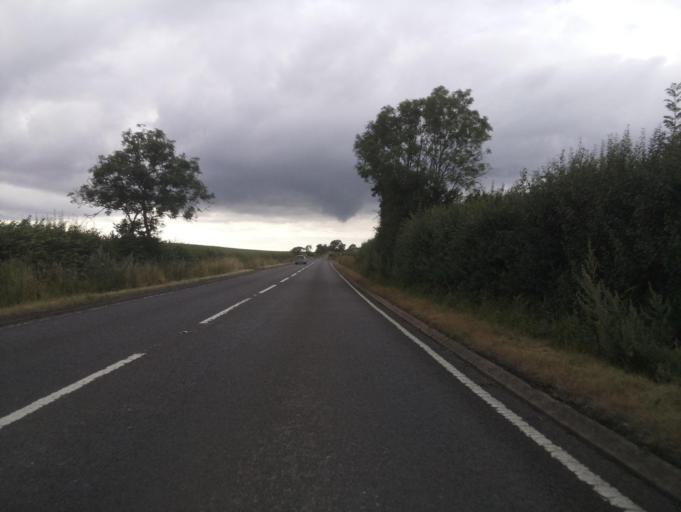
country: GB
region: England
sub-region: Warwickshire
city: Southam
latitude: 52.2045
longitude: -1.3853
